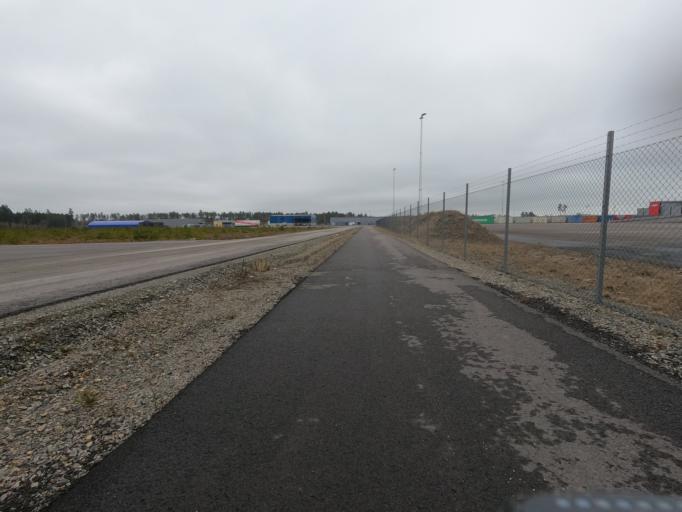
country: SE
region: Kronoberg
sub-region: Ljungby Kommun
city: Ljungby
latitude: 56.8285
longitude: 13.8984
